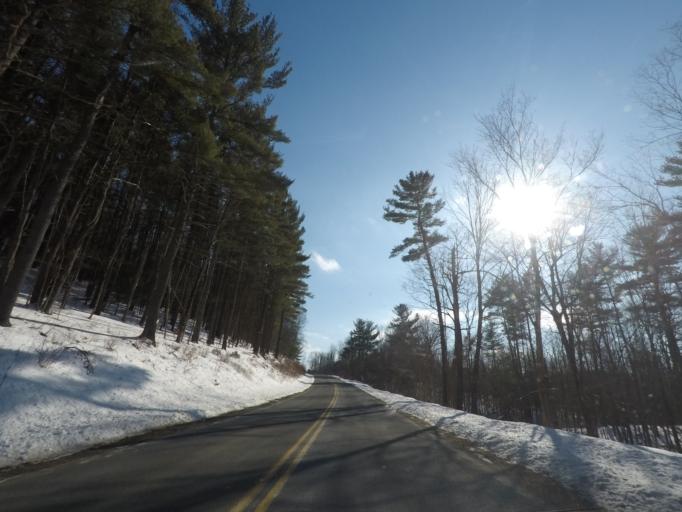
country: US
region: New York
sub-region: Rensselaer County
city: Hoosick Falls
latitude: 42.8892
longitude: -73.4957
